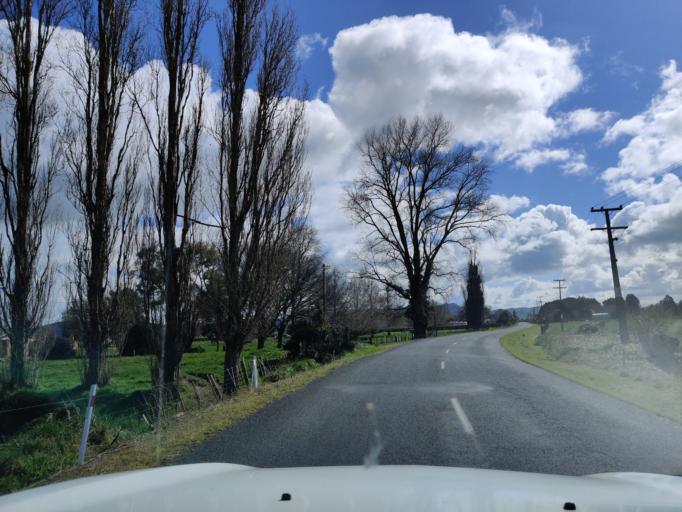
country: NZ
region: Waikato
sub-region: Waikato District
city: Ngaruawahia
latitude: -37.5766
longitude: 175.2693
